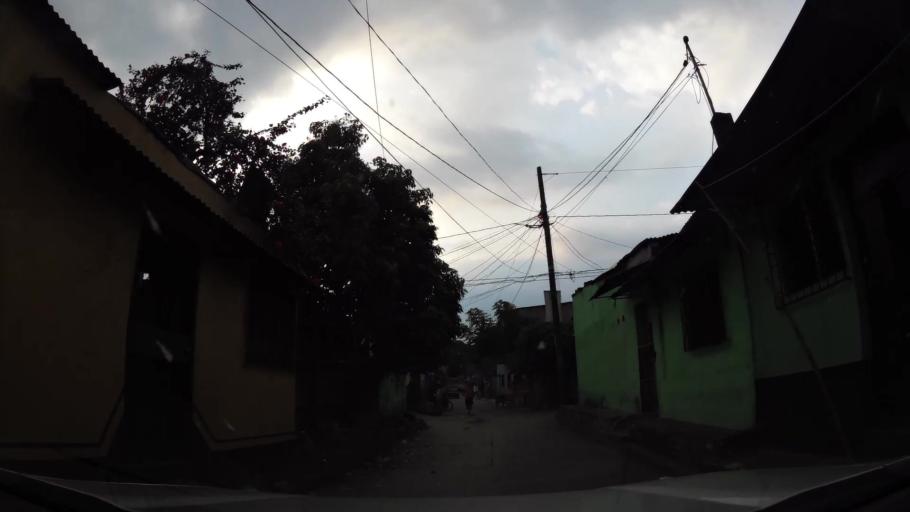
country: GT
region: Escuintla
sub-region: Municipio de Escuintla
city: Escuintla
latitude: 14.2860
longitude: -90.7803
